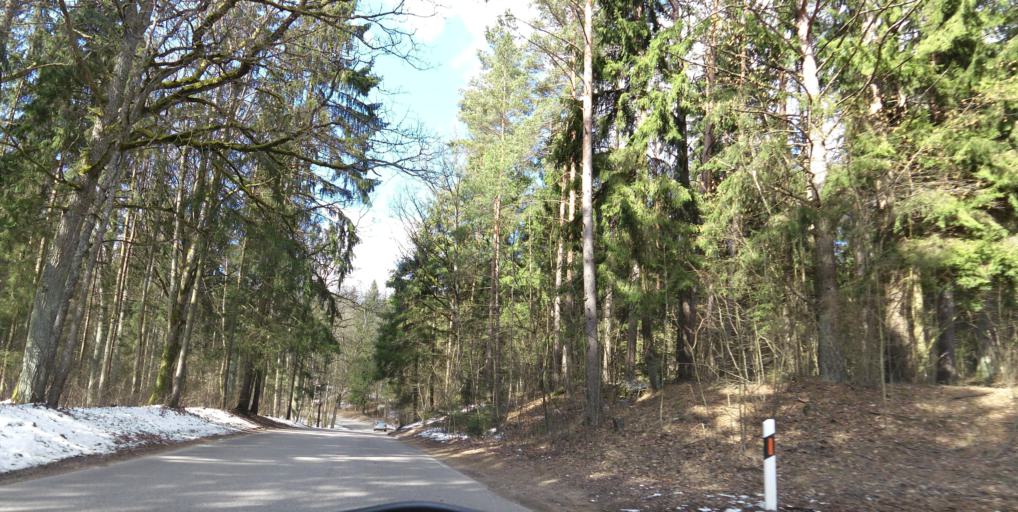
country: LT
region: Vilnius County
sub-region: Vilnius
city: Fabijoniskes
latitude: 54.7518
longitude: 25.3008
